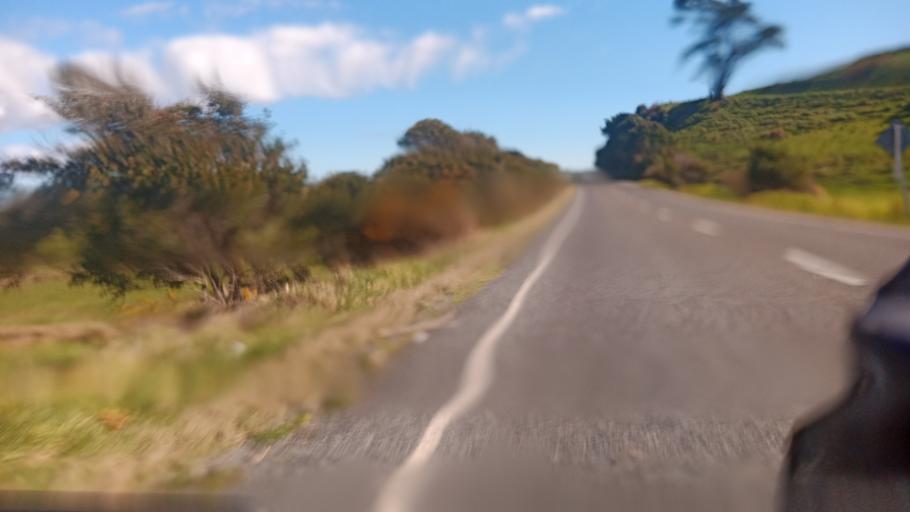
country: NZ
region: Bay of Plenty
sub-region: Opotiki District
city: Opotiki
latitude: -37.9903
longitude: 177.3469
